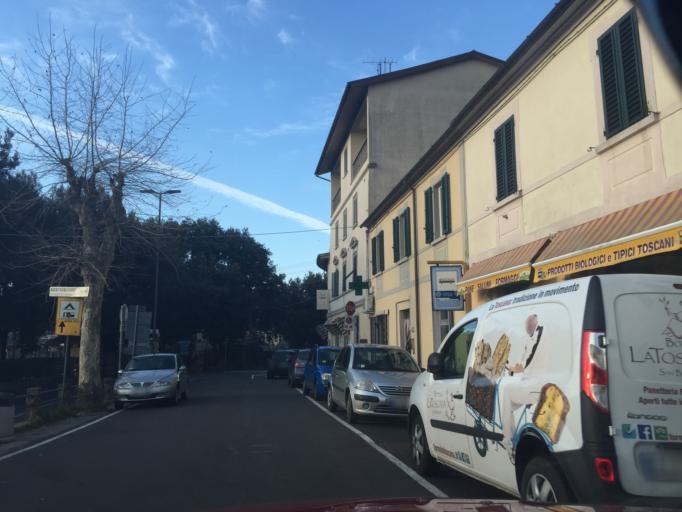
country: IT
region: Tuscany
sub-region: Provincia di Pistoia
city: Larciano
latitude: 43.8350
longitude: 10.9190
